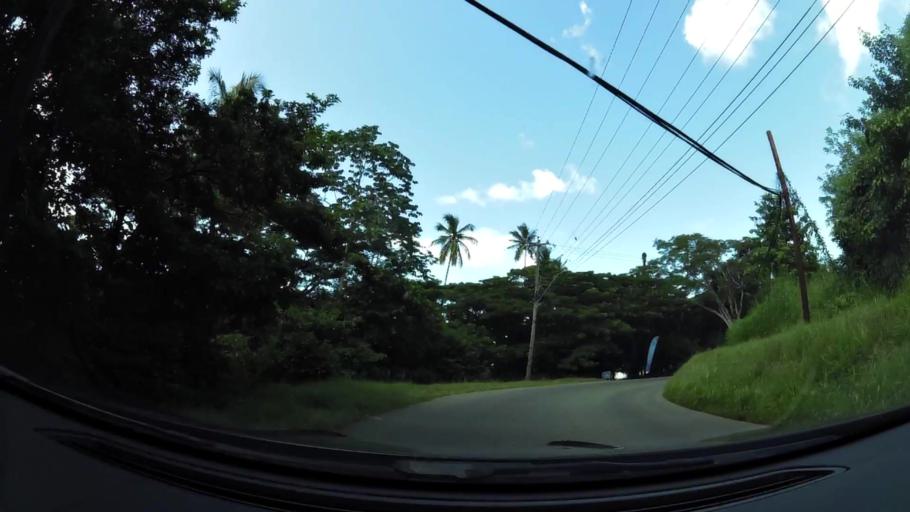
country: TT
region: Tobago
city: Scarborough
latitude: 11.2100
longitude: -60.7799
